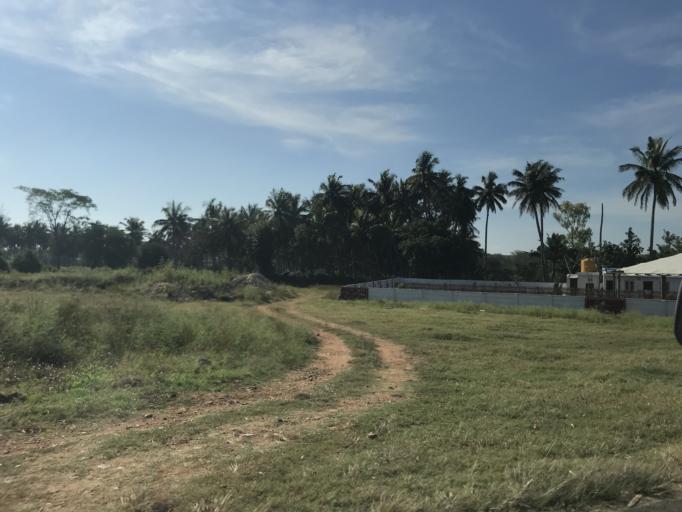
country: IN
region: Karnataka
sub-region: Mysore
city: Mysore
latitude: 12.1962
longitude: 76.5456
